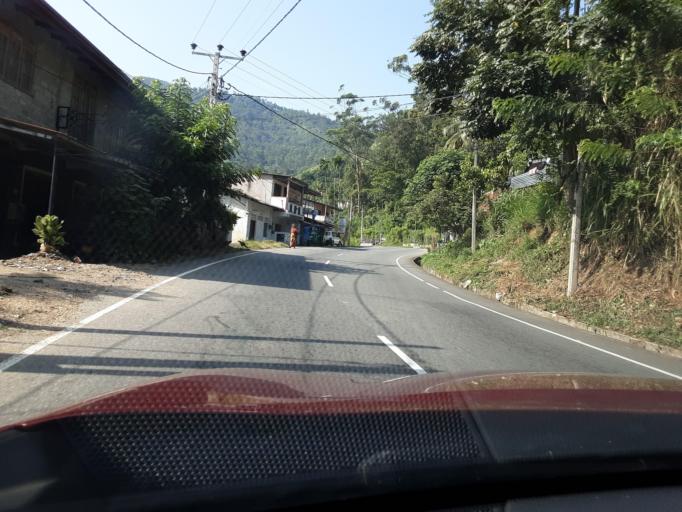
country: LK
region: Uva
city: Badulla
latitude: 6.9708
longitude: 81.0862
